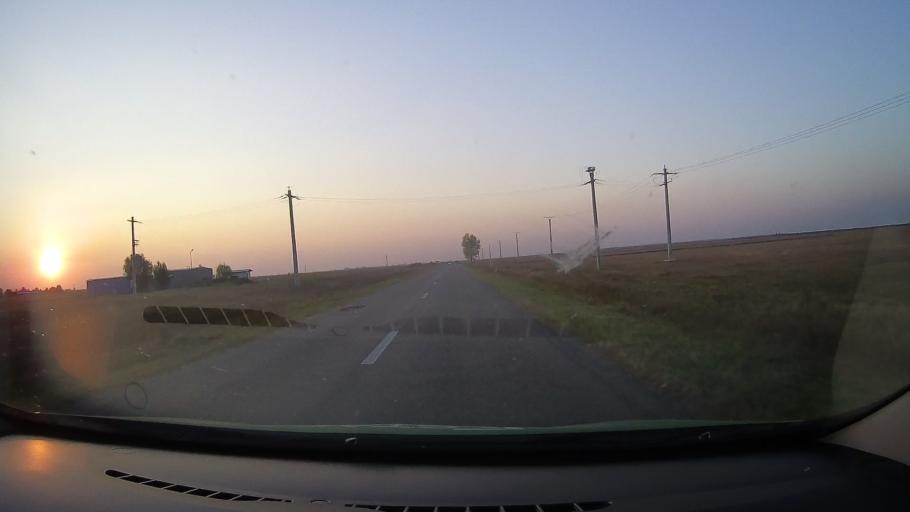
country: RO
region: Arad
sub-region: Comuna Zarand
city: Zarand
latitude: 46.4198
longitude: 21.6161
